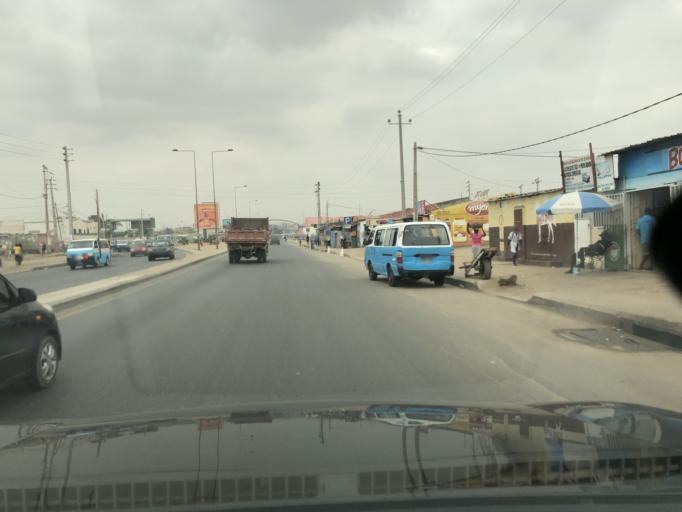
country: AO
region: Luanda
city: Luanda
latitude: -8.8339
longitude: 13.2832
